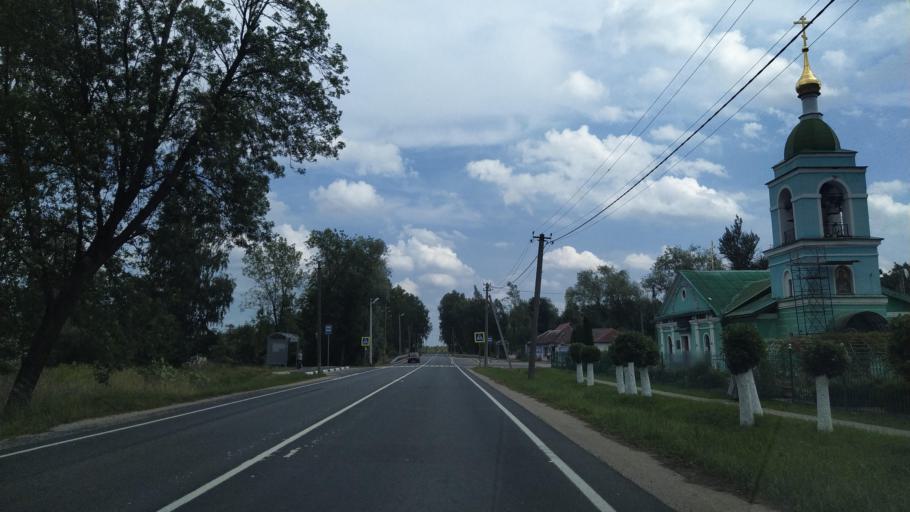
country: RU
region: Pskov
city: Pskov
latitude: 57.7614
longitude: 28.7607
